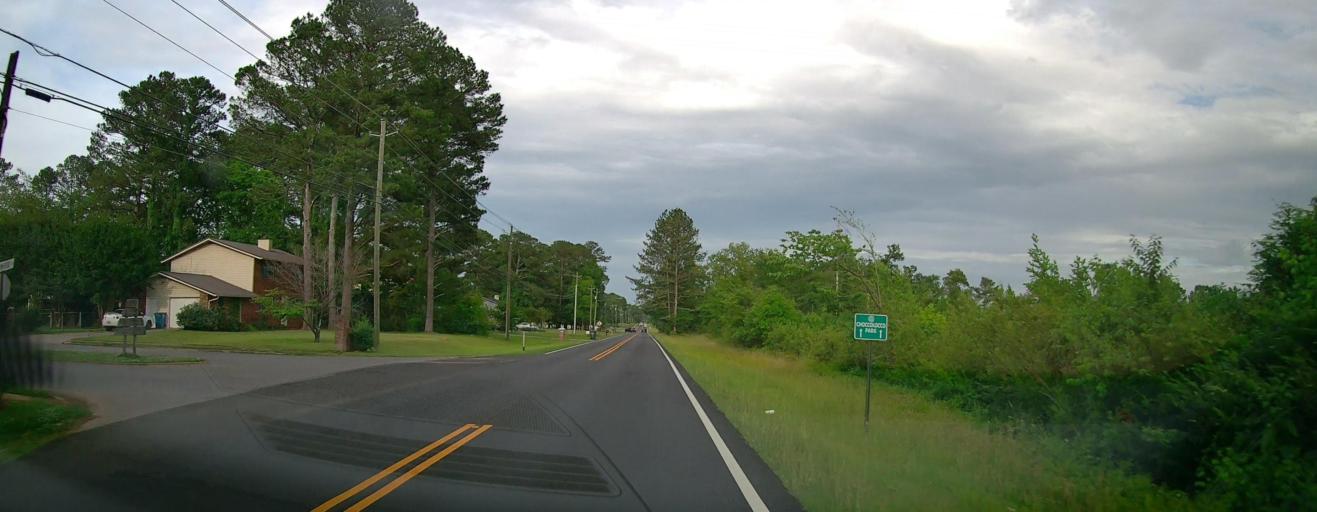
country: US
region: Alabama
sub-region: Calhoun County
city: Oxford
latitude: 33.5856
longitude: -85.7977
